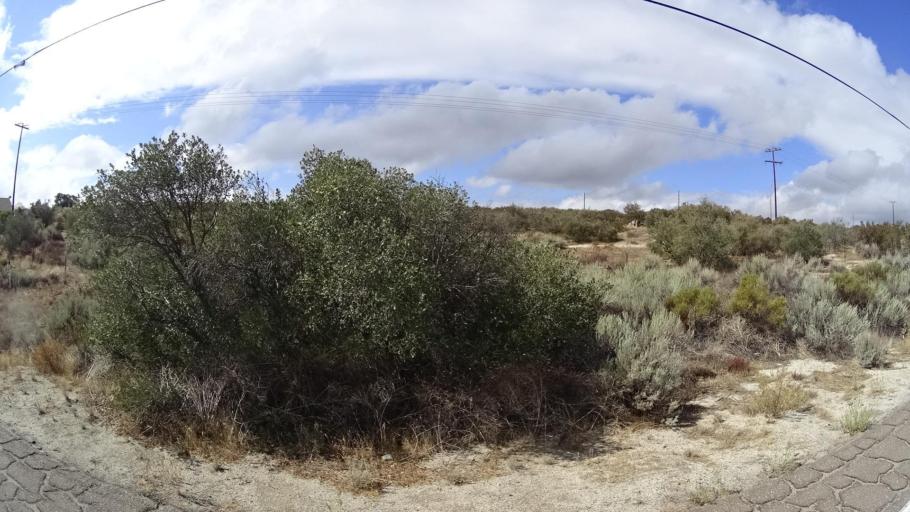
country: US
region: California
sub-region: San Diego County
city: Campo
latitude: 32.6917
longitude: -116.3412
